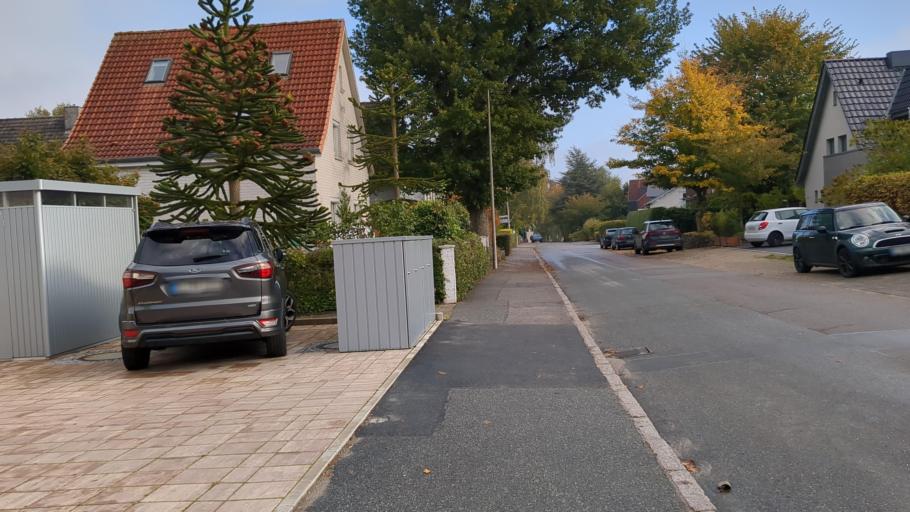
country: DE
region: Schleswig-Holstein
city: Wees
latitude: 54.8177
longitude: 9.4737
